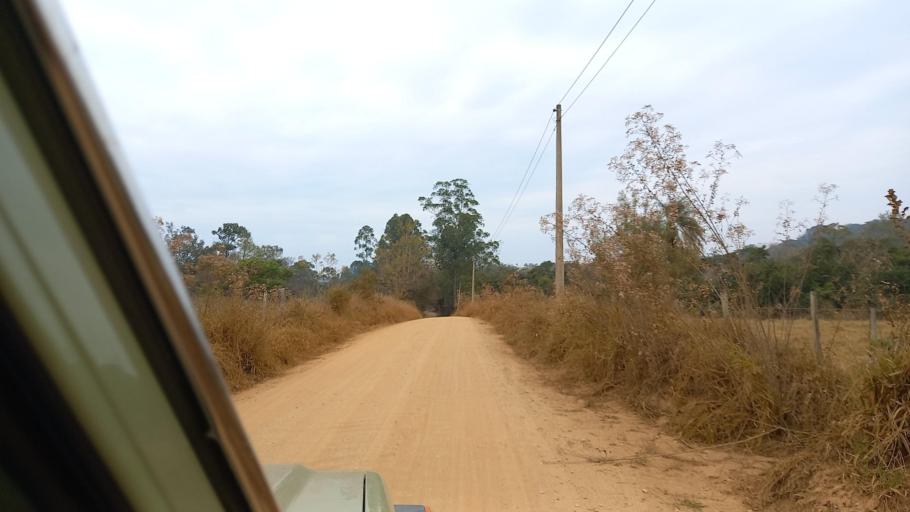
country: BR
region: Sao Paulo
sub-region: Moji-Guacu
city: Mogi-Gaucu
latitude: -22.3056
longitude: -46.8331
